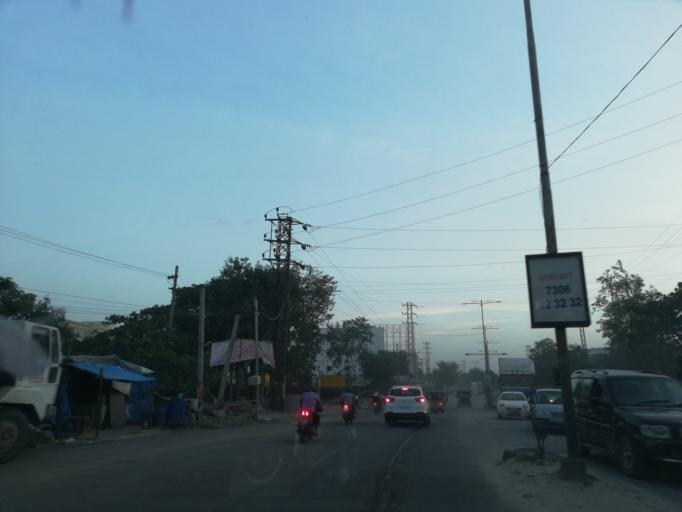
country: IN
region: Telangana
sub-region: Medak
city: Serilingampalle
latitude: 17.5347
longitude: 78.3578
